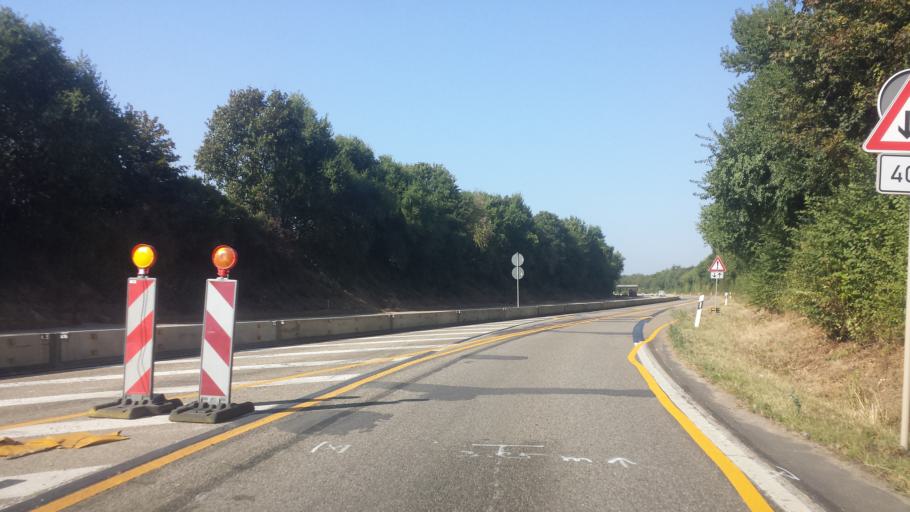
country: DE
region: Rheinland-Pfalz
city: Worms
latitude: 49.6220
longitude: 8.3320
